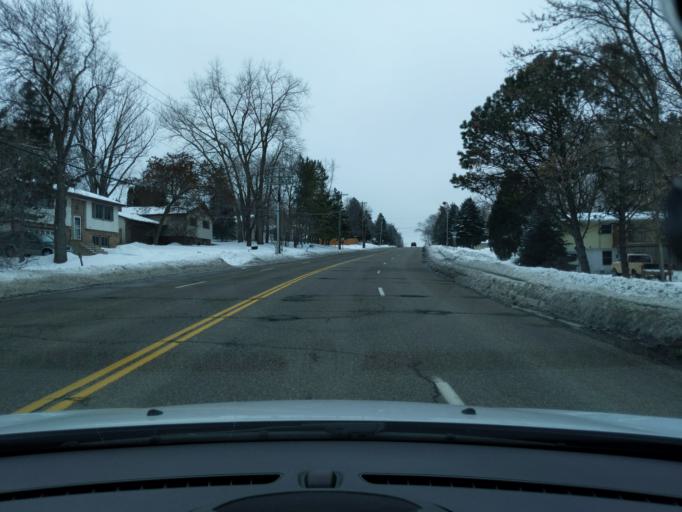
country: US
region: Minnesota
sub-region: Ramsey County
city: Roseville
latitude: 45.0206
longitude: -93.1359
